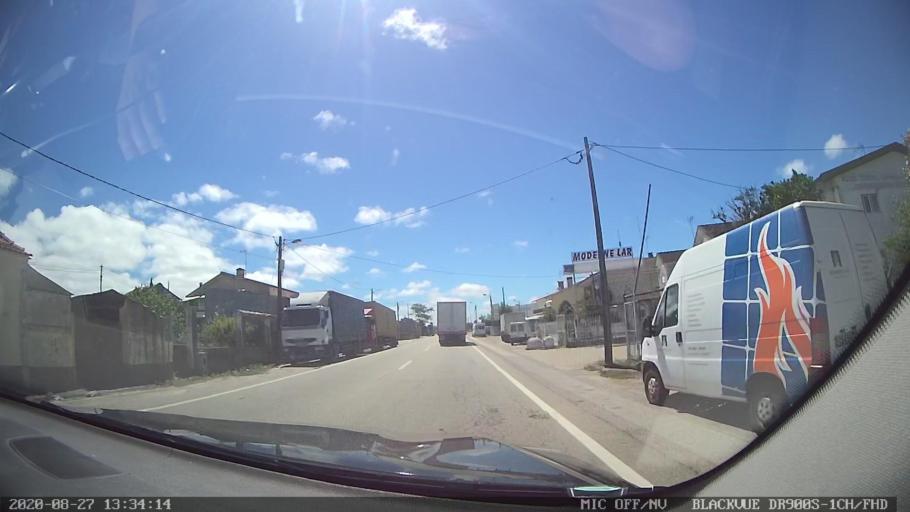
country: PT
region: Coimbra
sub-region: Mira
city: Mira
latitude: 40.4731
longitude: -8.6969
